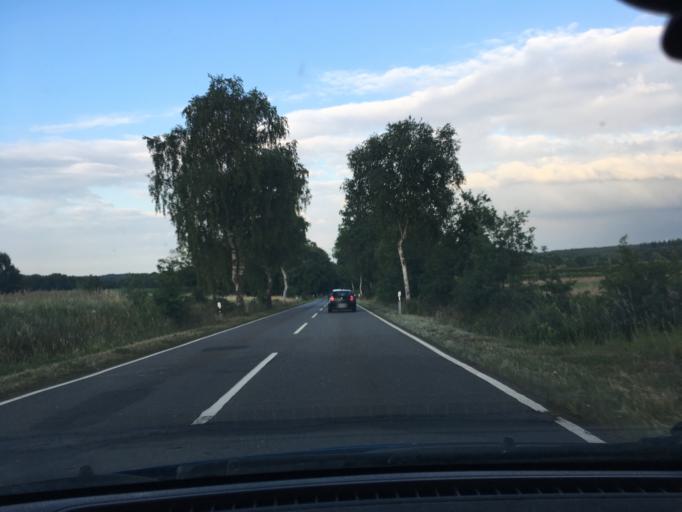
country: DE
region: Lower Saxony
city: Soderstorf
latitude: 53.1451
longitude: 10.1365
